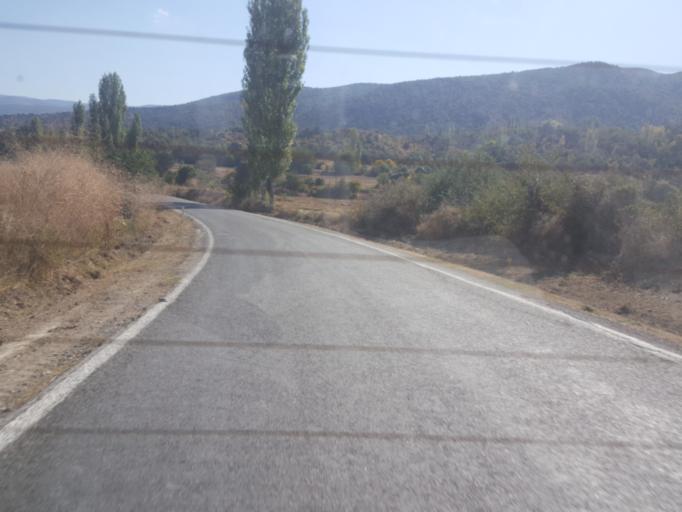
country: TR
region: Kastamonu
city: Tosya
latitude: 40.9920
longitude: 34.1220
